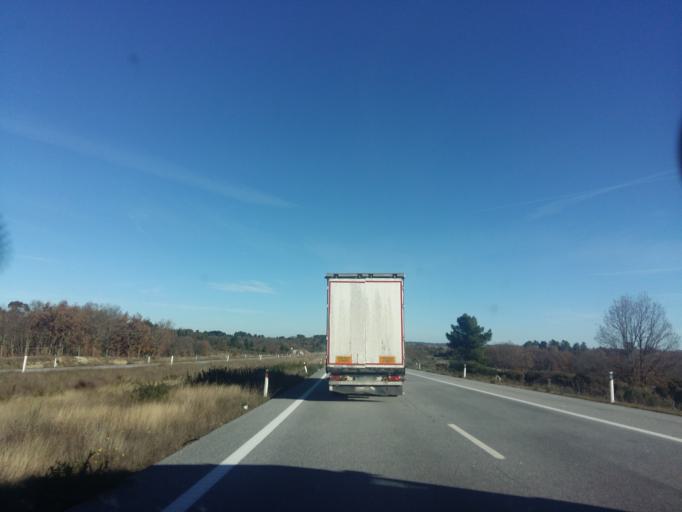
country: PT
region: Guarda
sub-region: Guarda
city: Sequeira
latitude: 40.6016
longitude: -7.0888
